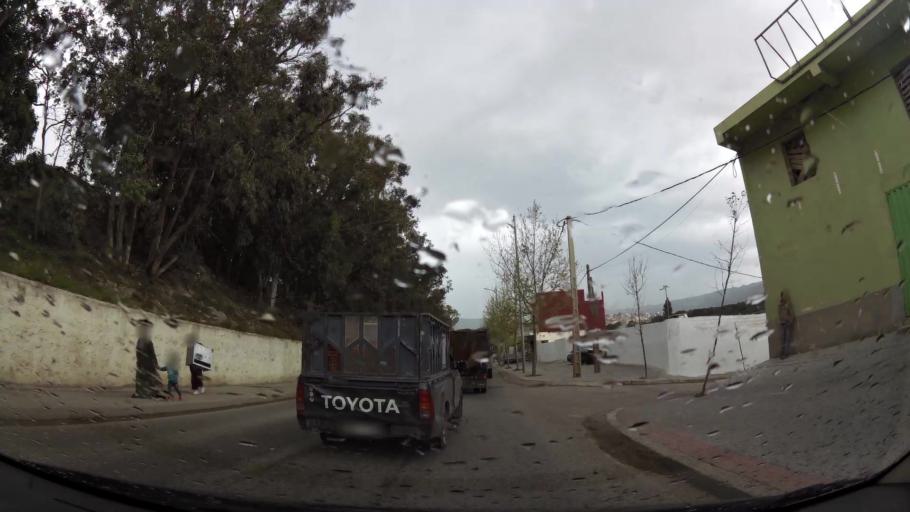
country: MA
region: Tanger-Tetouan
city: Tetouan
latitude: 35.5560
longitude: -5.4038
